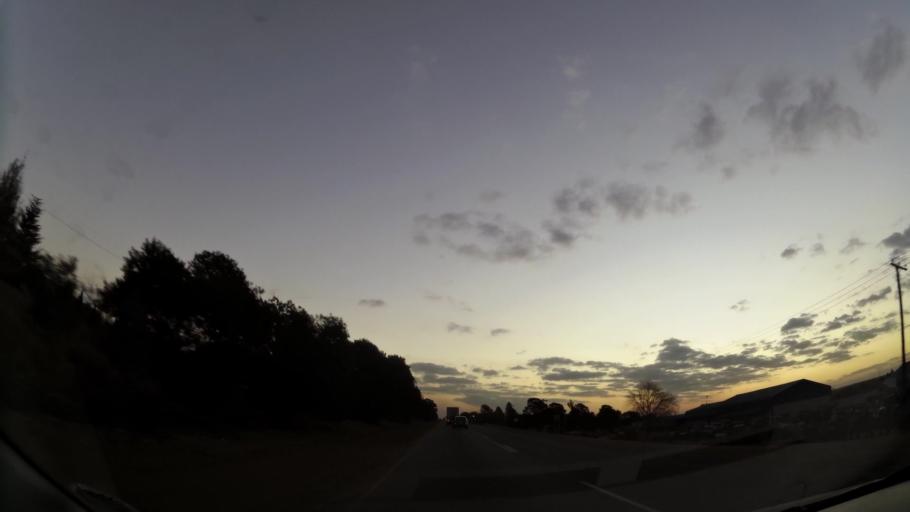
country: ZA
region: Gauteng
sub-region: West Rand District Municipality
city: Krugersdorp
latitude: -26.0691
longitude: 27.6825
